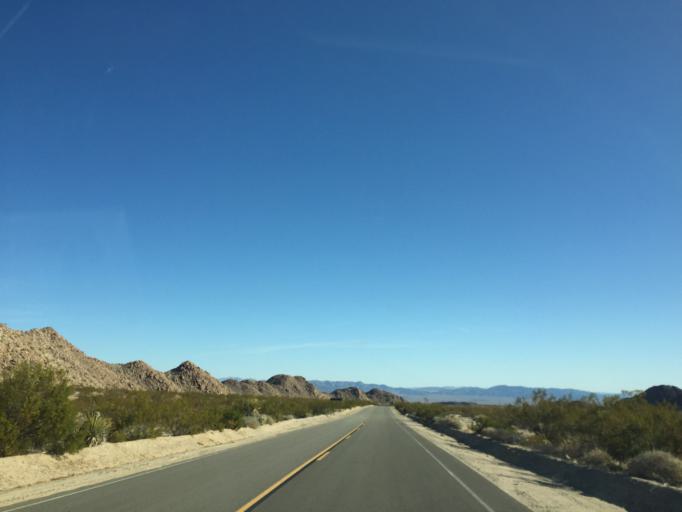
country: US
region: California
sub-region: Riverside County
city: Mecca
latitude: 33.8211
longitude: -115.7622
